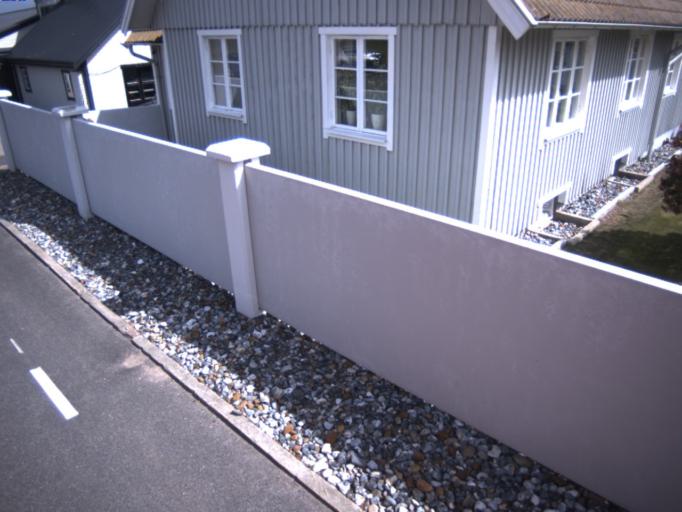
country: SE
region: Skane
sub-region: Helsingborg
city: Odakra
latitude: 56.0898
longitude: 12.6977
